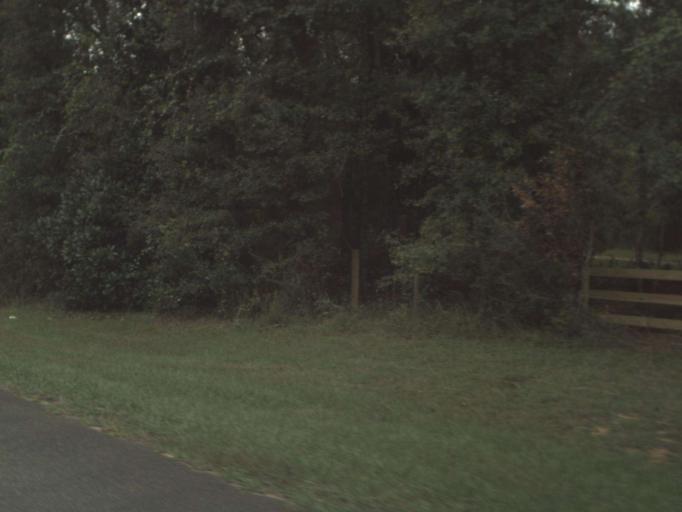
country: US
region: Florida
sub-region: Jackson County
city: Sneads
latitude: 30.6144
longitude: -85.0297
